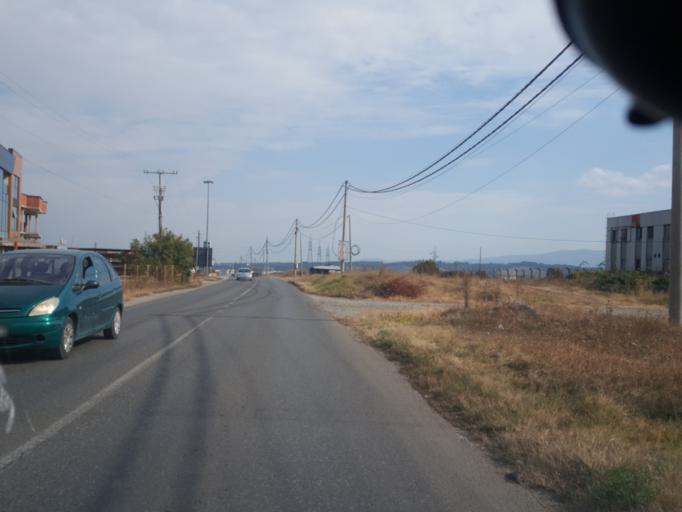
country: XK
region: Gjakova
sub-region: Komuna e Gjakoves
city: Gjakove
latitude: 42.3692
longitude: 20.4577
